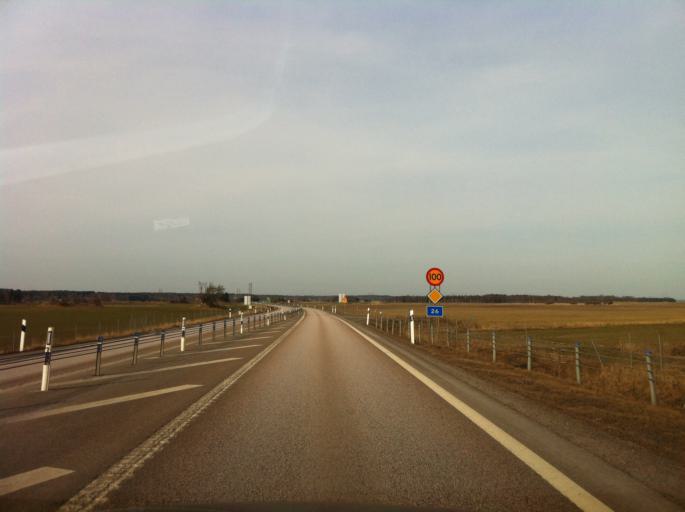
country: SE
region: Vaestra Goetaland
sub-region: Skovde Kommun
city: Stopen
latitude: 58.5513
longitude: 13.8093
